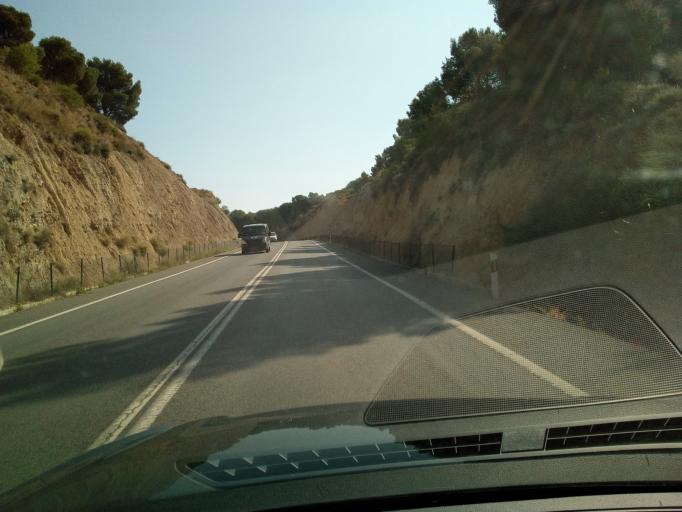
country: ES
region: Navarre
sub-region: Provincia de Navarra
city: Cadreita
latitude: 42.2175
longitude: -1.6607
